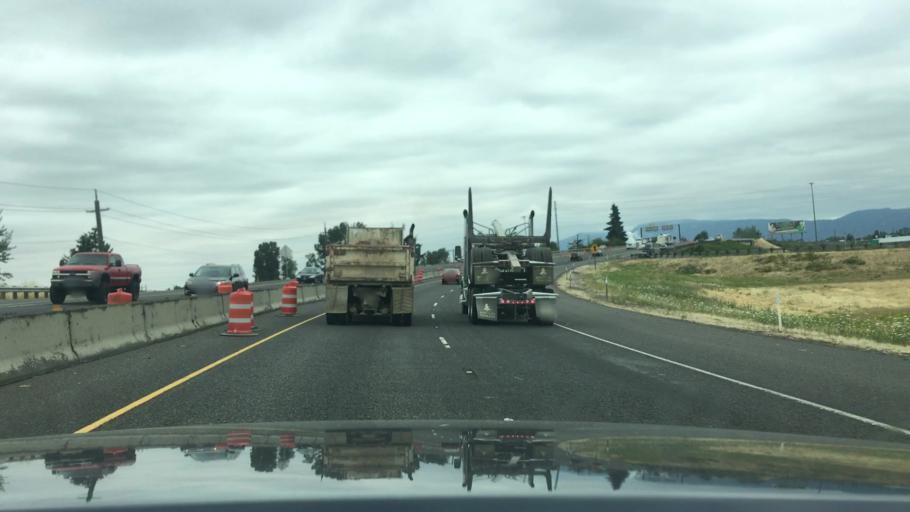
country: US
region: Oregon
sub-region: Lane County
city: Eugene
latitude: 44.0946
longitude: -123.1698
